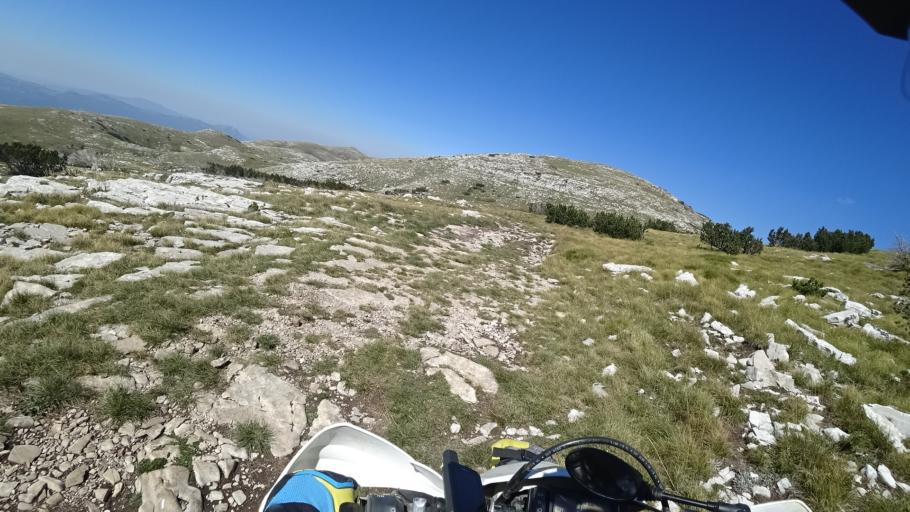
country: HR
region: Splitsko-Dalmatinska
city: Hrvace
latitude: 43.9344
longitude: 16.5715
